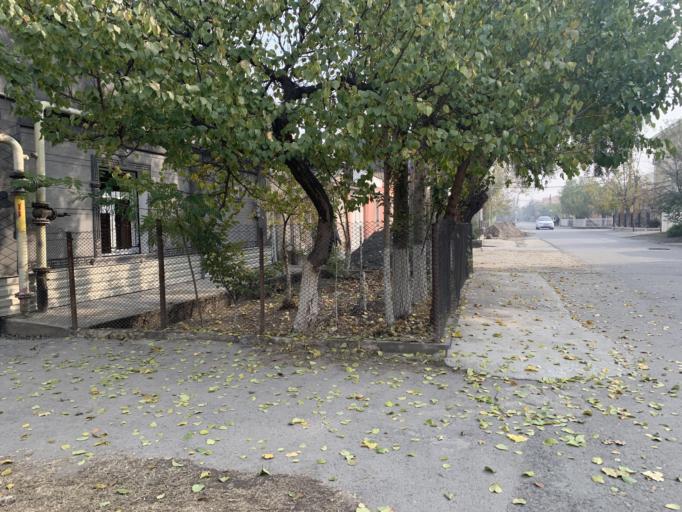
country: UZ
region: Fergana
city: Qo`qon
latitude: 40.5450
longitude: 70.9265
